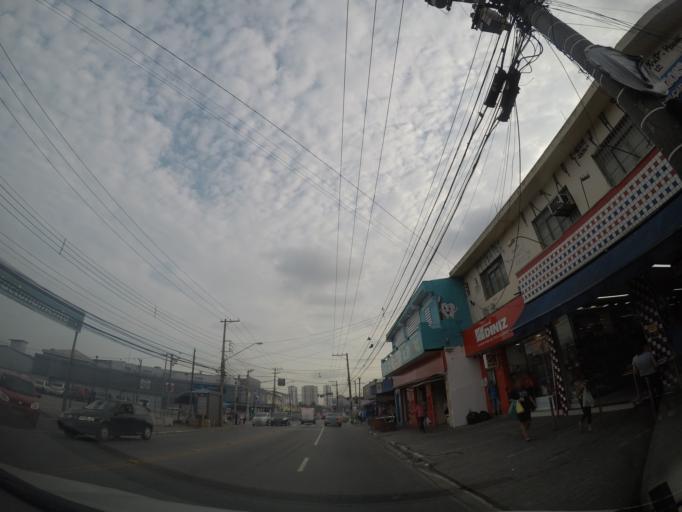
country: BR
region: Sao Paulo
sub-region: Guarulhos
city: Guarulhos
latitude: -23.4478
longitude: -46.5085
